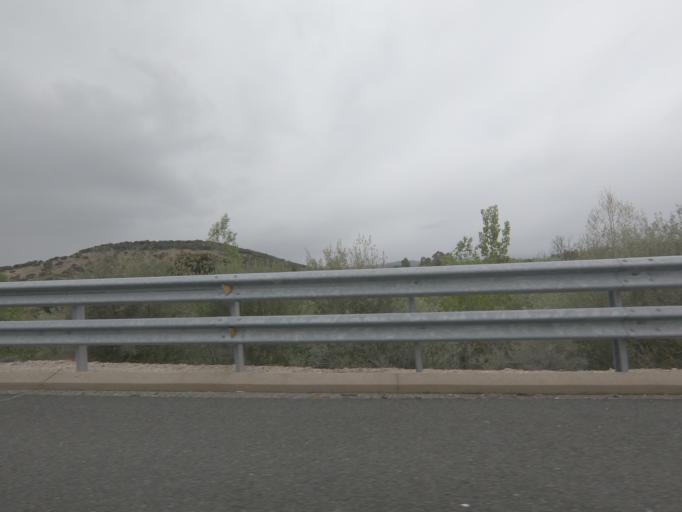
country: ES
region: Extremadura
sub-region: Provincia de Caceres
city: Jarilla
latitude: 40.1623
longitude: -6.0252
